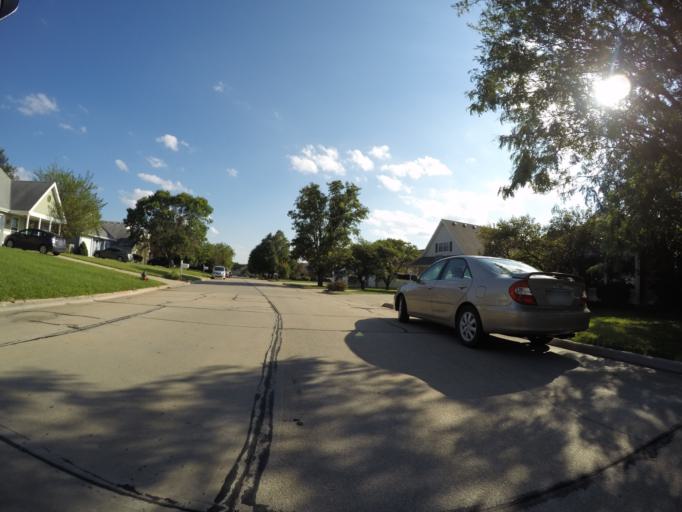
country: US
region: Kansas
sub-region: Riley County
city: Manhattan
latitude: 39.2013
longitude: -96.6295
